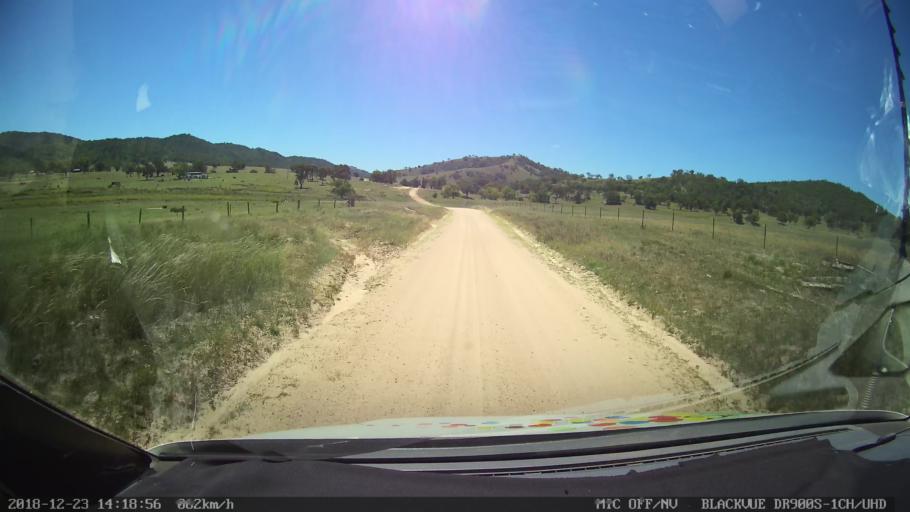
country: AU
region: New South Wales
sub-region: Tamworth Municipality
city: Manilla
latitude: -30.6553
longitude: 150.9997
